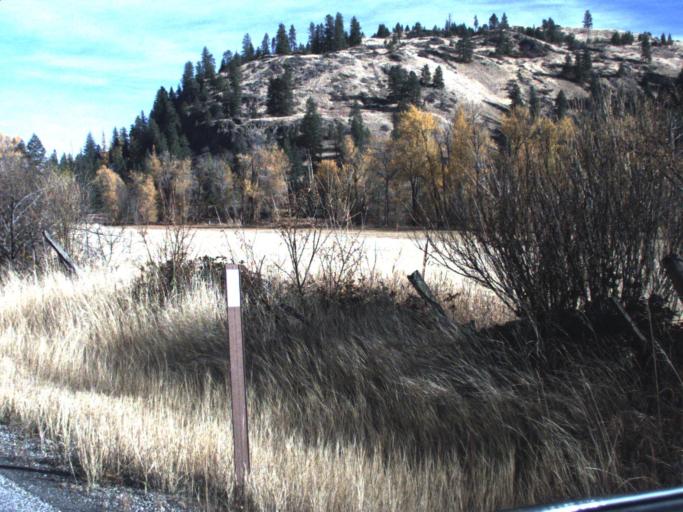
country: CA
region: British Columbia
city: Grand Forks
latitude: 48.9352
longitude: -118.5591
